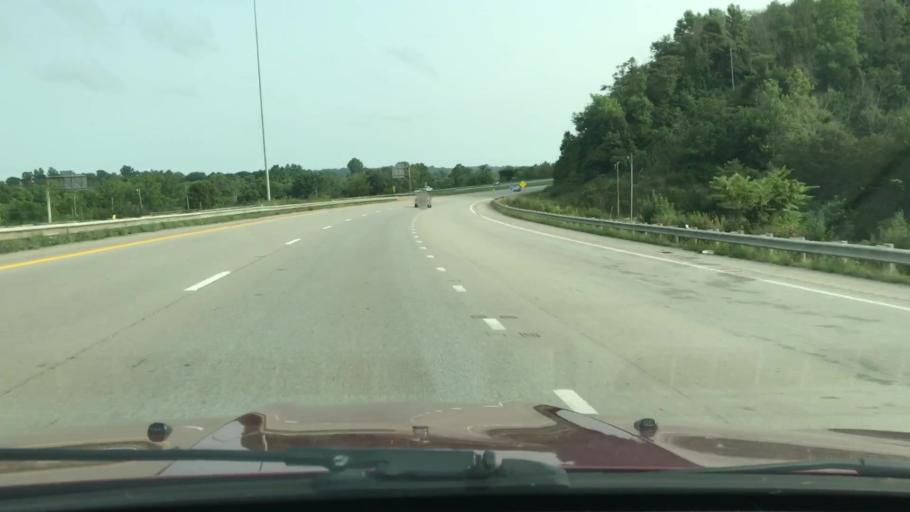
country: US
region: Ohio
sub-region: Guernsey County
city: Cambridge
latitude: 40.0032
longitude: -81.5603
